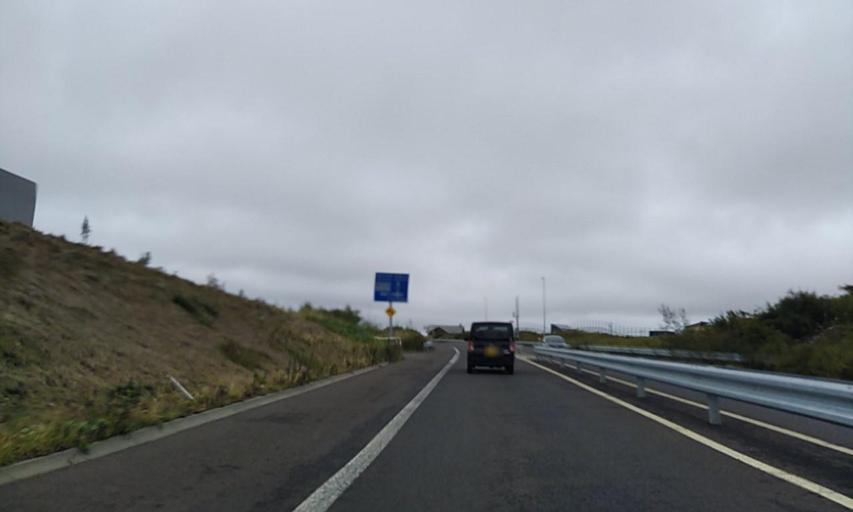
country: JP
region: Hokkaido
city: Nemuro
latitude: 43.3135
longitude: 145.5486
